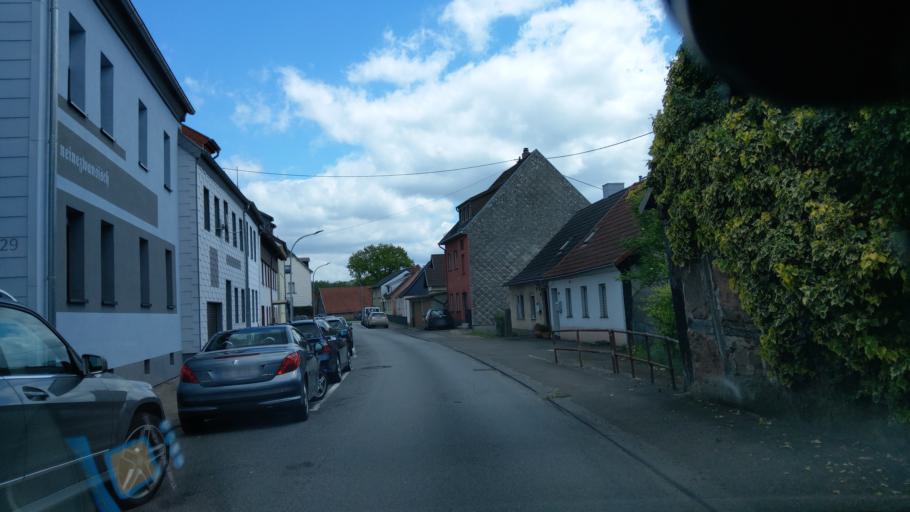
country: DE
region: Saarland
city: Neunkirchen
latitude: 49.3729
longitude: 7.1810
